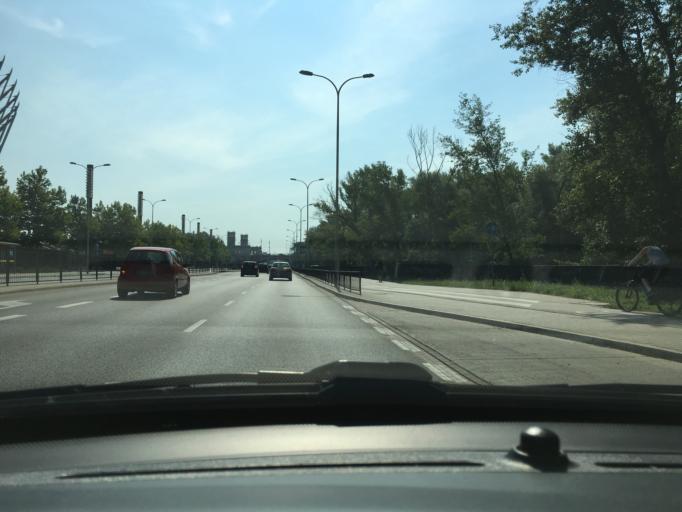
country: PL
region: Masovian Voivodeship
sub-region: Warszawa
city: Praga Polnoc
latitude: 52.2398
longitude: 21.0415
